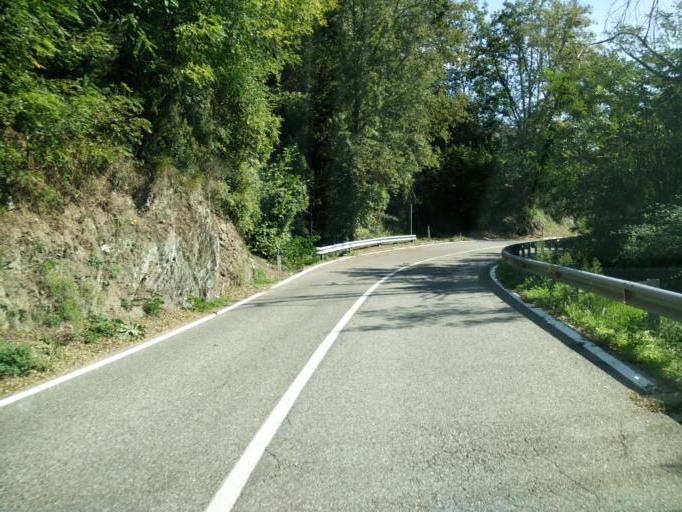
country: IT
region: Liguria
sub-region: Provincia di La Spezia
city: Carrodano
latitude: 44.2458
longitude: 9.6360
